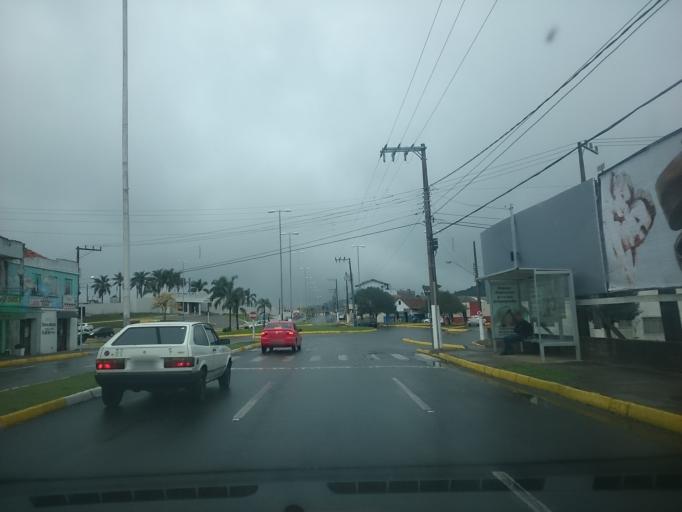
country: BR
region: Santa Catarina
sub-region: Lages
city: Lages
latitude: -27.8261
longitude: -50.3355
